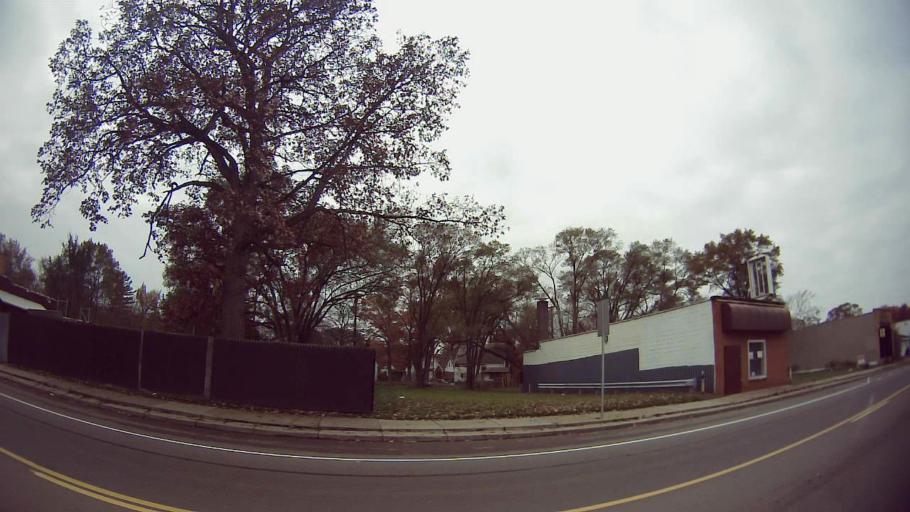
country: US
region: Michigan
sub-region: Oakland County
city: Hazel Park
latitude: 42.4394
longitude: -83.0783
